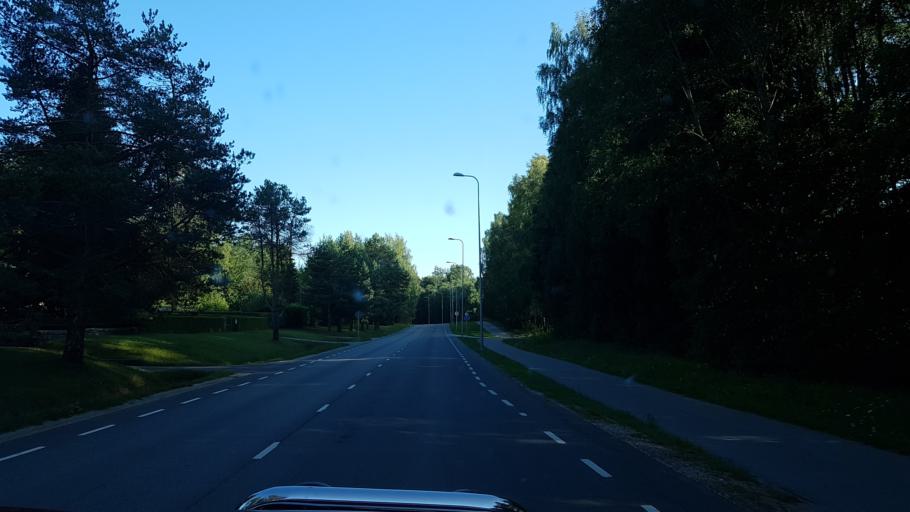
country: EE
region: Harju
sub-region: Raasiku vald
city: Raasiku
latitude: 59.1756
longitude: 25.1700
